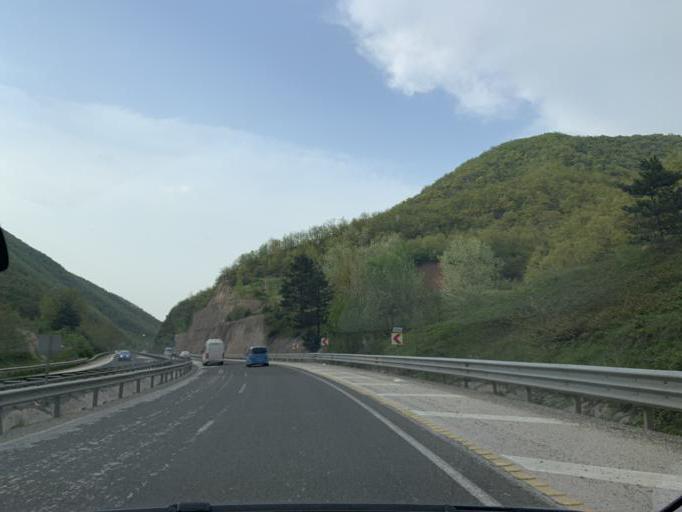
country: TR
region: Bursa
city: Kursunlu
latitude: 39.9971
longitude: 29.6538
